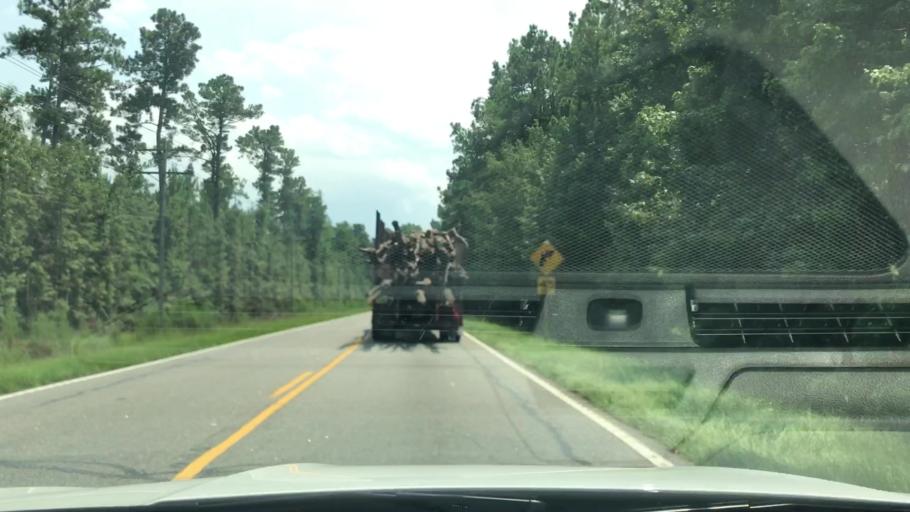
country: US
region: South Carolina
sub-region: Georgetown County
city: Georgetown
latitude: 33.4403
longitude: -79.2767
